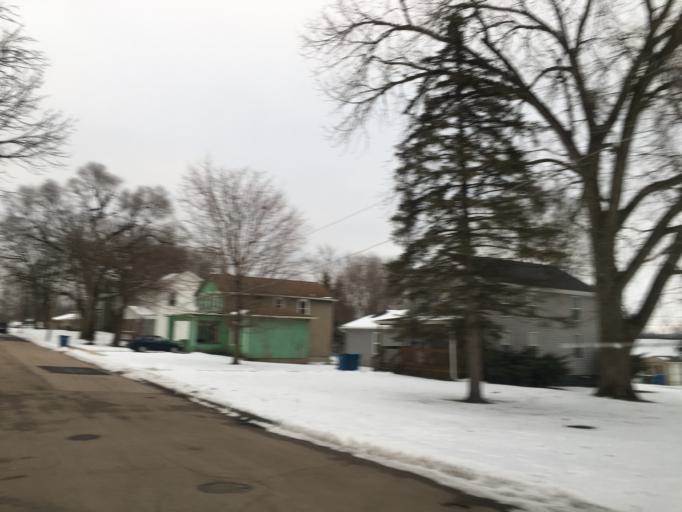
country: US
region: Illinois
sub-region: LaSalle County
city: Peru
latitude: 41.3265
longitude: -89.1251
